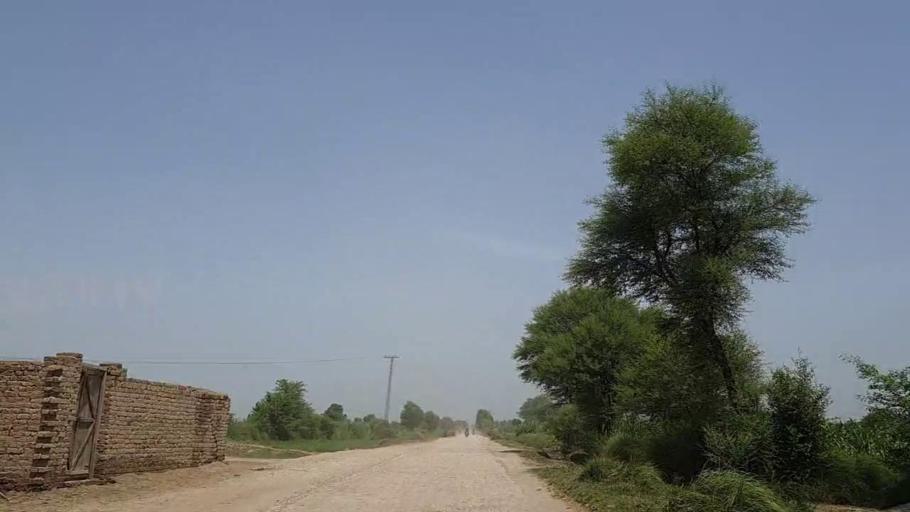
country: PK
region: Sindh
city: Tharu Shah
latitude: 26.8971
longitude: 68.0089
